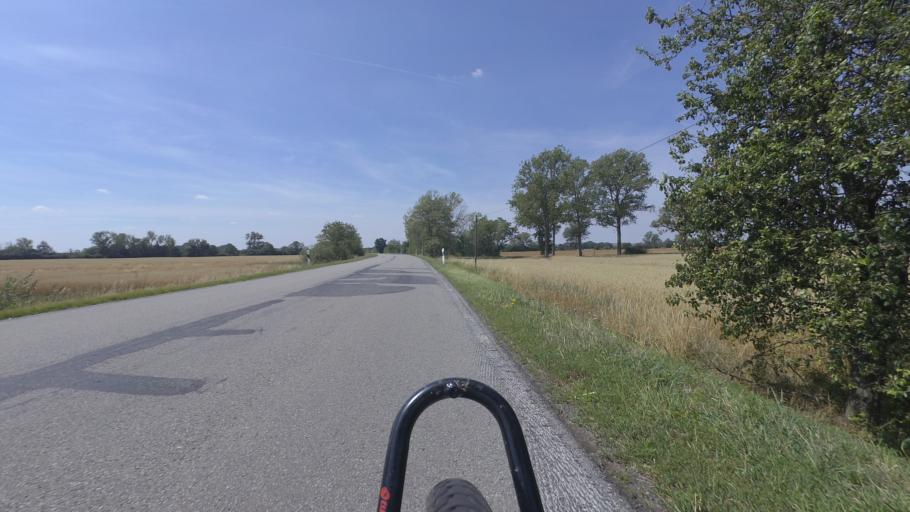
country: DE
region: Saxony-Anhalt
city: Schollene
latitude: 52.7688
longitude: 12.2062
